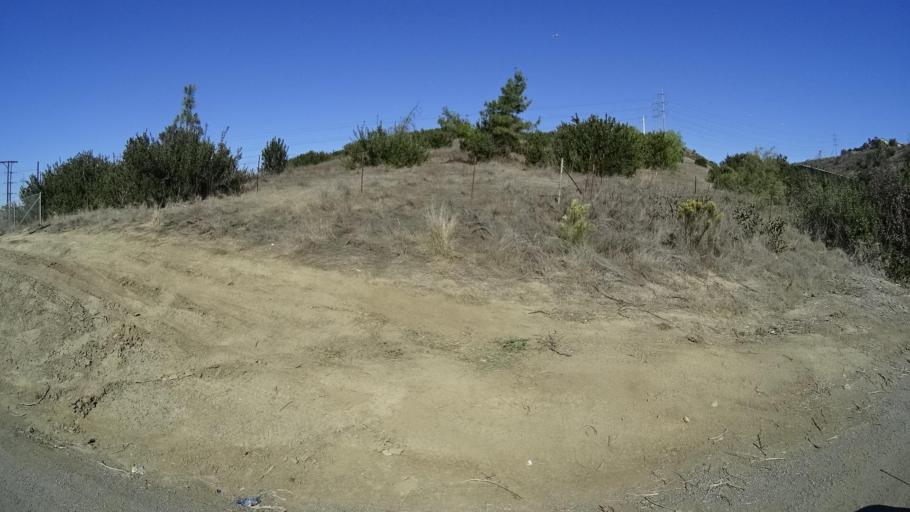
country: US
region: California
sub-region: San Diego County
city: La Presa
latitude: 32.6649
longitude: -116.9851
